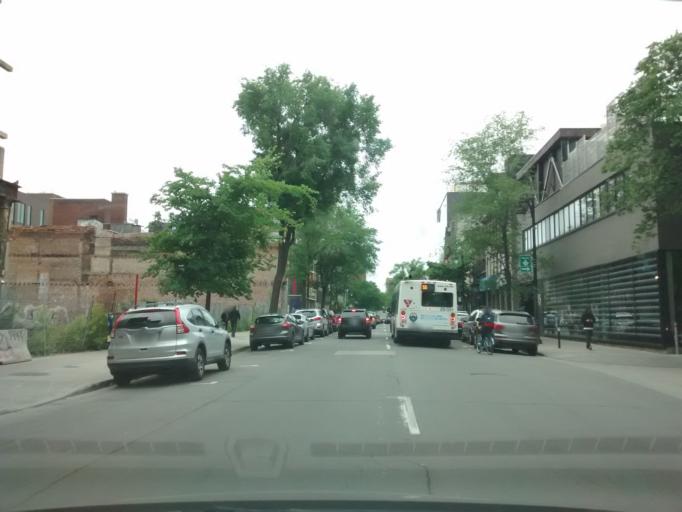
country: CA
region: Quebec
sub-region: Montreal
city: Montreal
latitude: 45.5092
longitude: -73.5624
